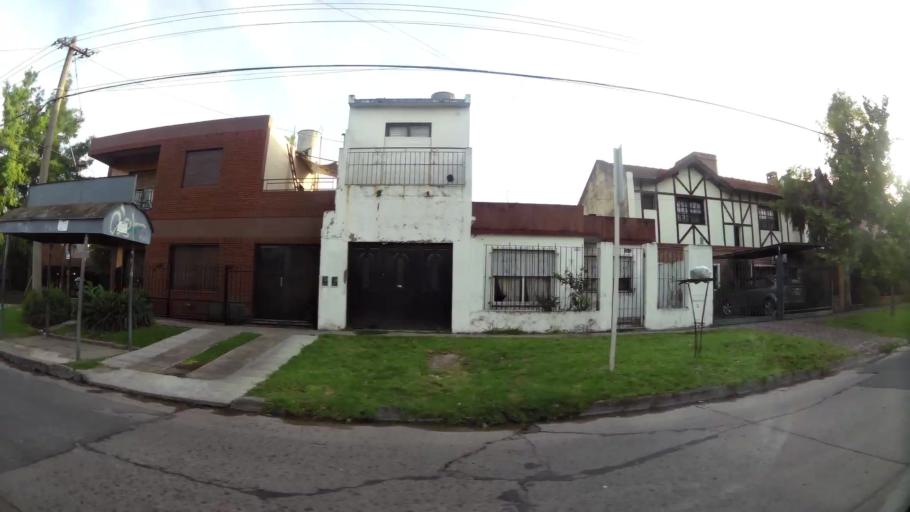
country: AR
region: Buenos Aires
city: Ituzaingo
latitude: -34.6405
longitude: -58.6534
